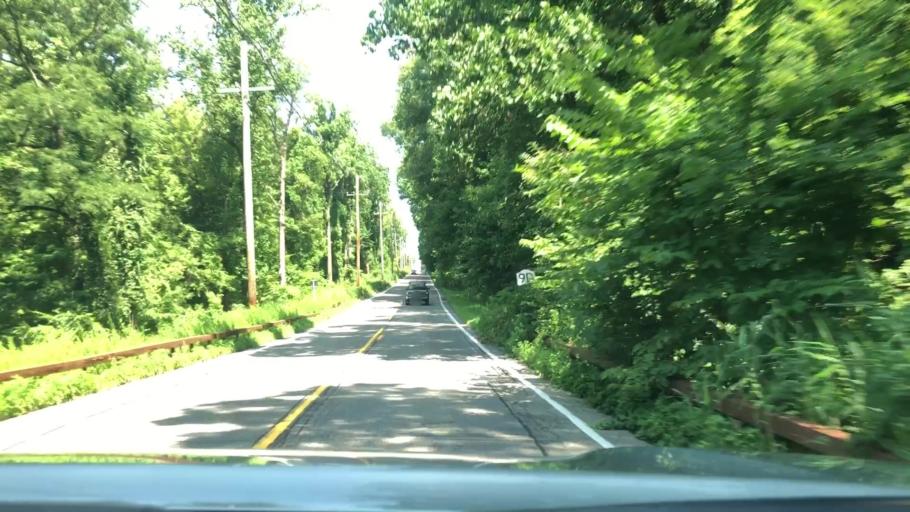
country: US
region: New York
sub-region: Orange County
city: Cornwall-on-Hudson
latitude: 41.4532
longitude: -73.9821
